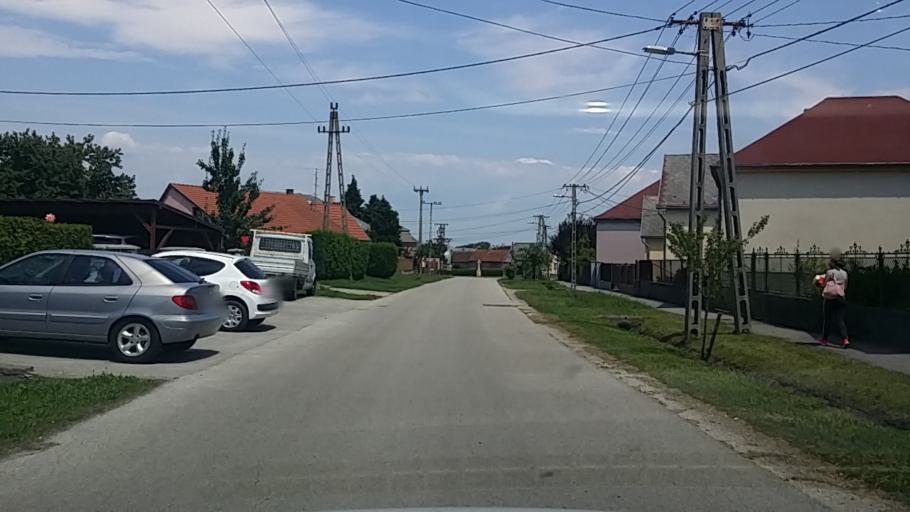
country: HU
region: Zala
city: Nagykanizsa
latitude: 46.4488
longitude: 16.9570
